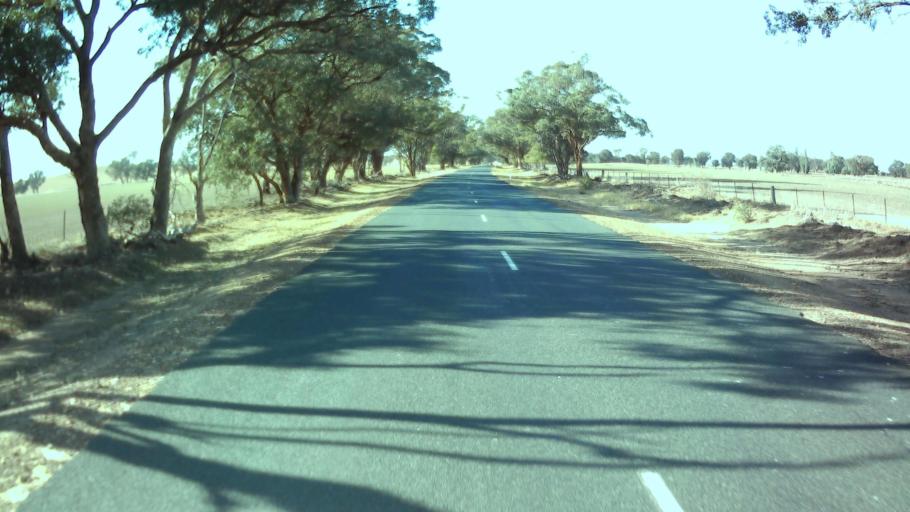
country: AU
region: New South Wales
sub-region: Weddin
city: Grenfell
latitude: -33.9569
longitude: 148.1395
